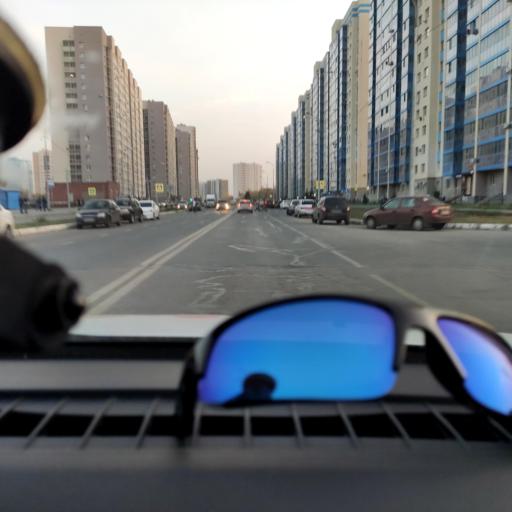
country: RU
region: Samara
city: Rozhdestveno
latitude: 53.1539
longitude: 50.0752
